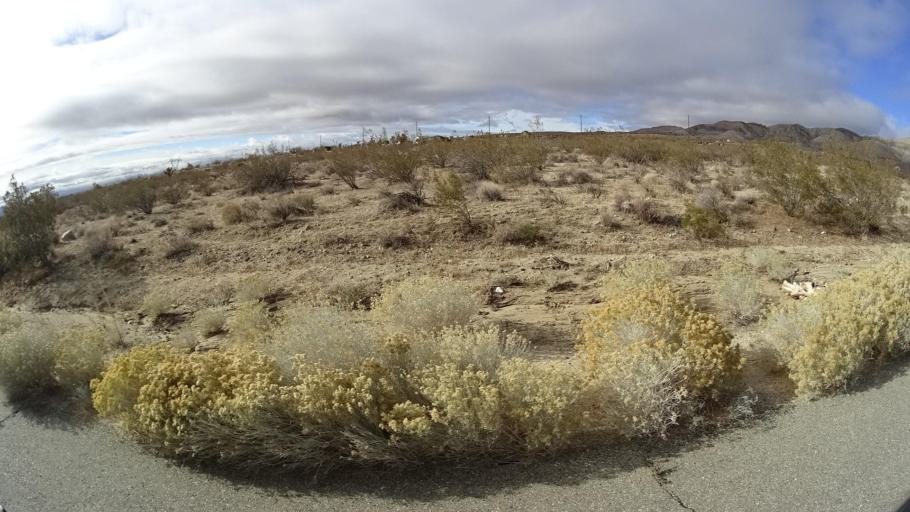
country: US
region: California
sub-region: Kern County
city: Mojave
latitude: 34.9919
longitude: -118.3252
